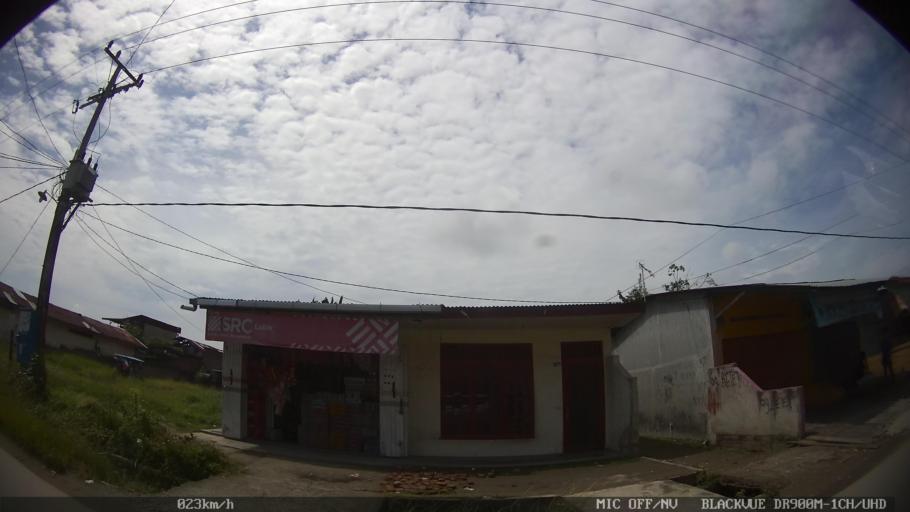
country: ID
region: North Sumatra
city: Medan
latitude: 3.5908
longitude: 98.7510
